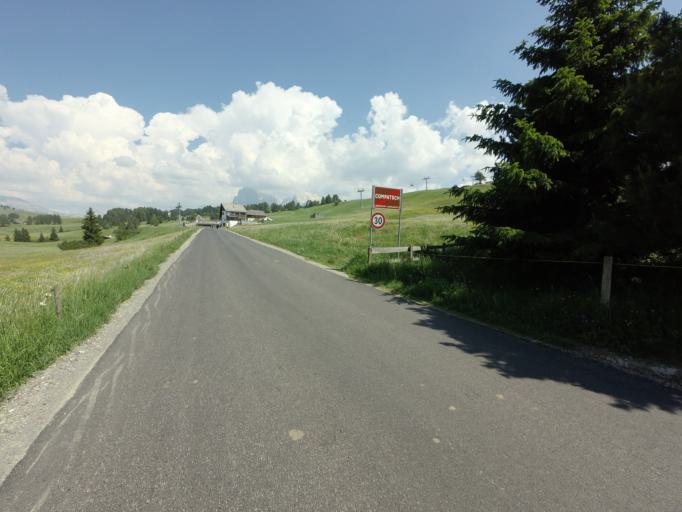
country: IT
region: Trentino-Alto Adige
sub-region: Bolzano
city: Ortisei
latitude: 46.5402
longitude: 11.6210
